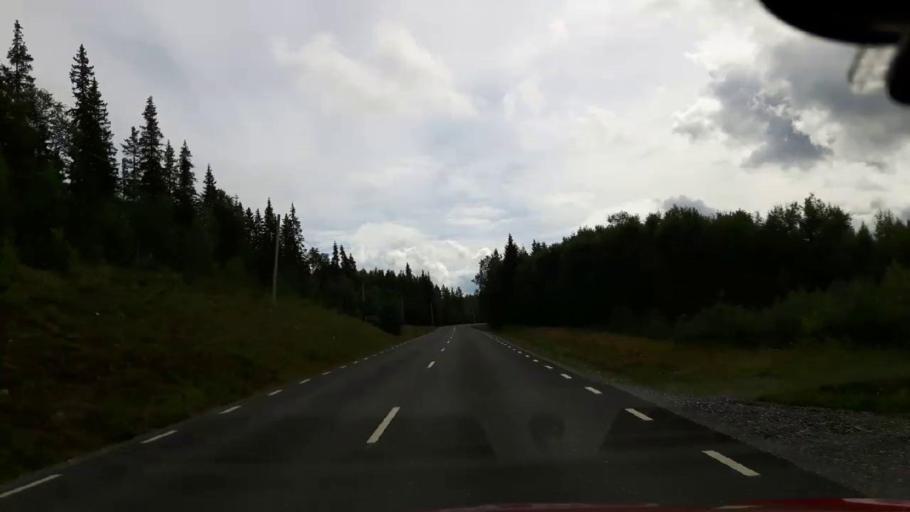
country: NO
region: Nord-Trondelag
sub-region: Lierne
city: Sandvika
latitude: 64.5888
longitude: 14.1201
